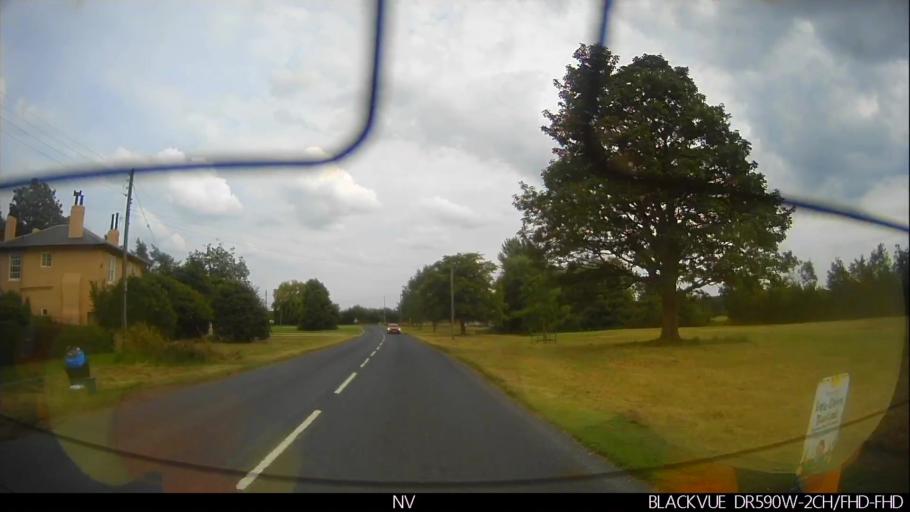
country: GB
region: England
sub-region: City of York
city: Holtby
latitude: 54.0503
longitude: -0.9610
